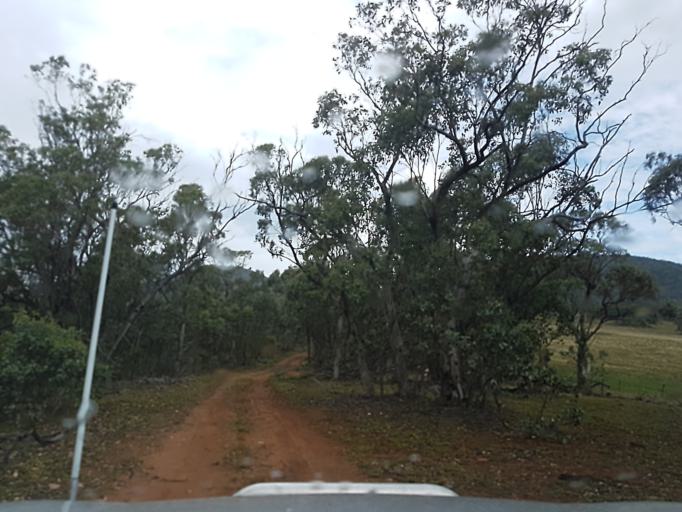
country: AU
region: New South Wales
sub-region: Snowy River
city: Jindabyne
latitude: -36.9637
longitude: 148.3825
